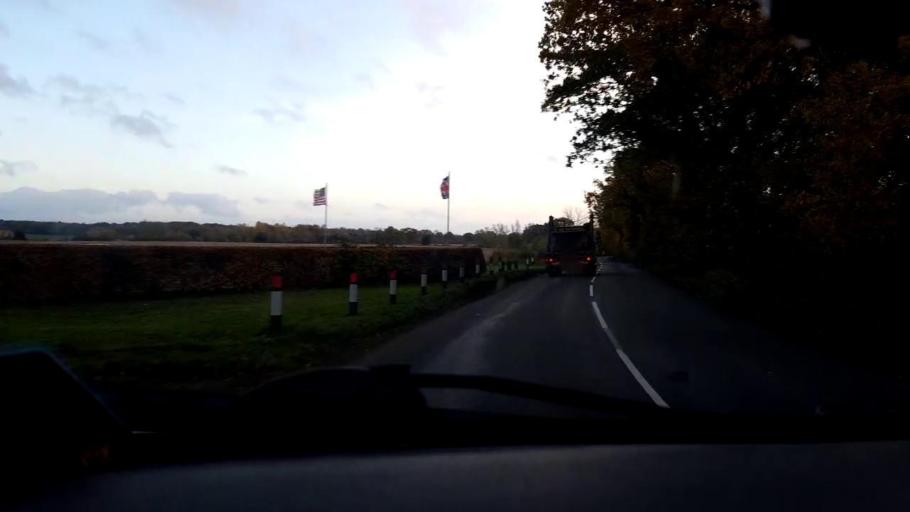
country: GB
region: England
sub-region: Norfolk
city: Mattishall
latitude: 52.6890
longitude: 1.1016
